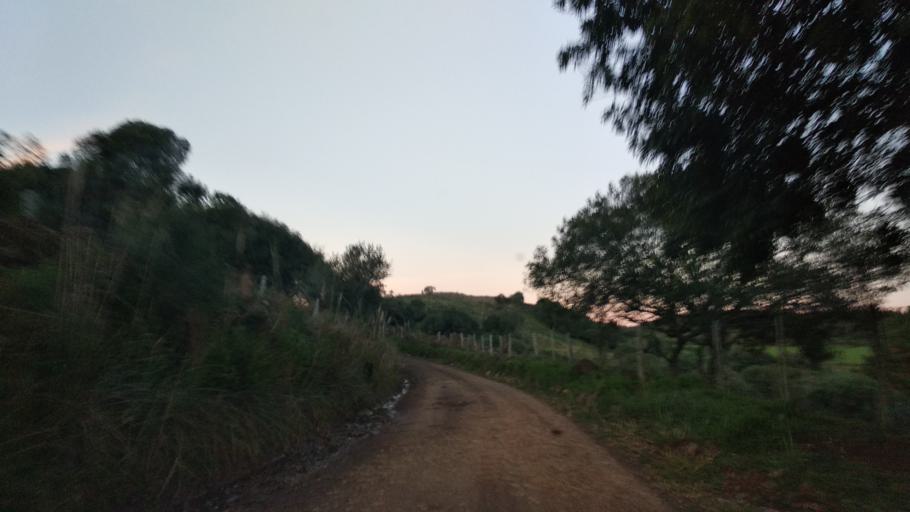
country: BR
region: Santa Catarina
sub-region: Celso Ramos
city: Celso Ramos
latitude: -27.5581
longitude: -51.2248
